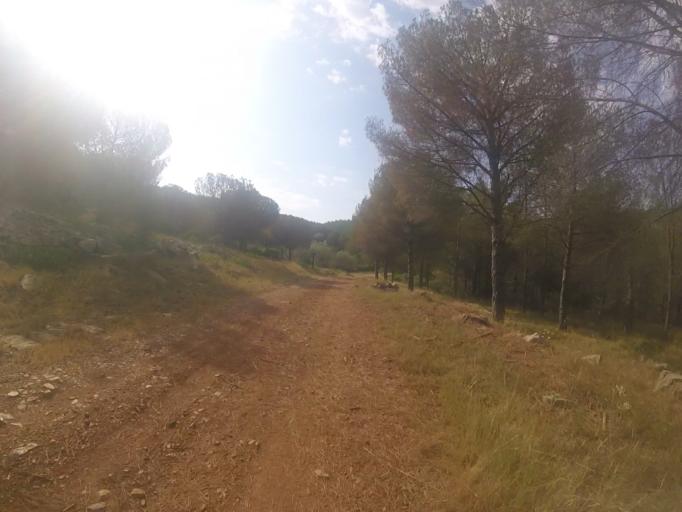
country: ES
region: Valencia
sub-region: Provincia de Castello
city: Cervera del Maestre
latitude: 40.3966
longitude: 0.2073
